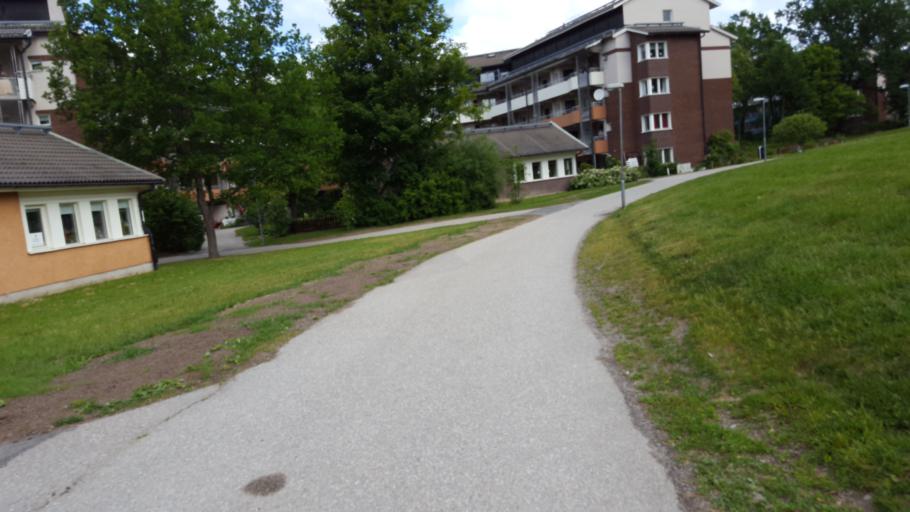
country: SE
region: Stockholm
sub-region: Upplands Vasby Kommun
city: Upplands Vaesby
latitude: 59.5123
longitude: 17.8823
